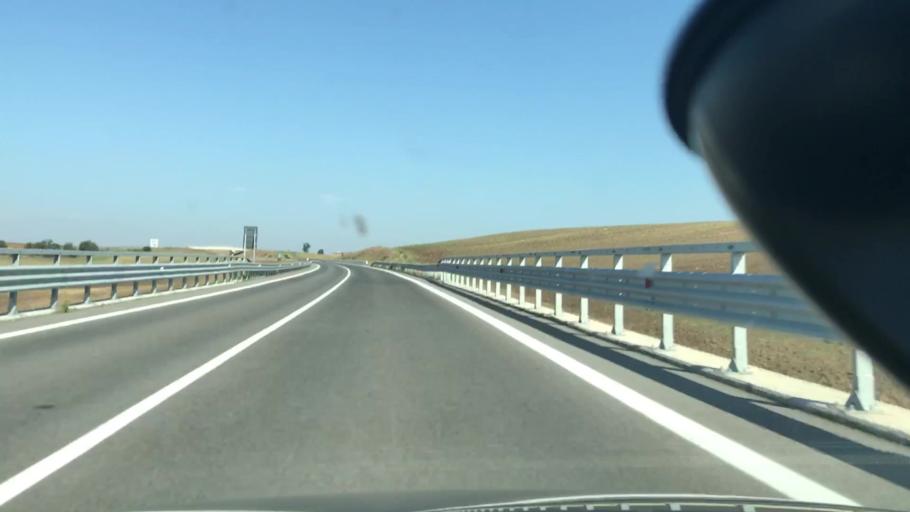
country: IT
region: Basilicate
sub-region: Provincia di Potenza
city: Palazzo San Gervasio
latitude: 40.9634
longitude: 16.0108
